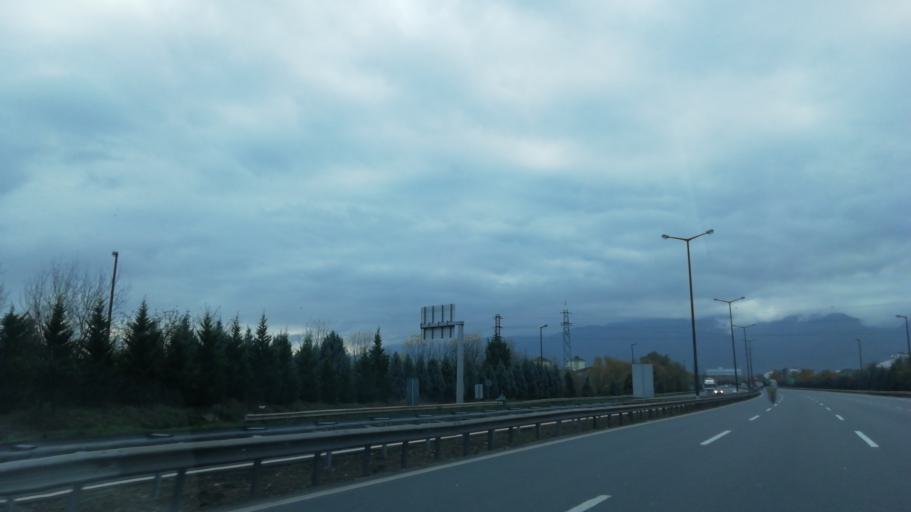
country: TR
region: Kocaeli
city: Kosekoy
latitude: 40.7457
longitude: 30.0418
